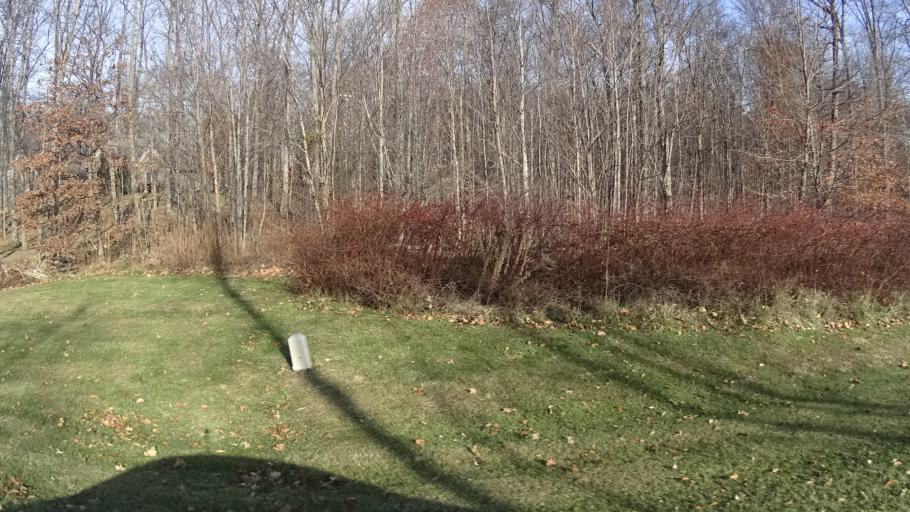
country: US
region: Ohio
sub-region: Lorain County
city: Grafton
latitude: 41.2186
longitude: -82.0366
